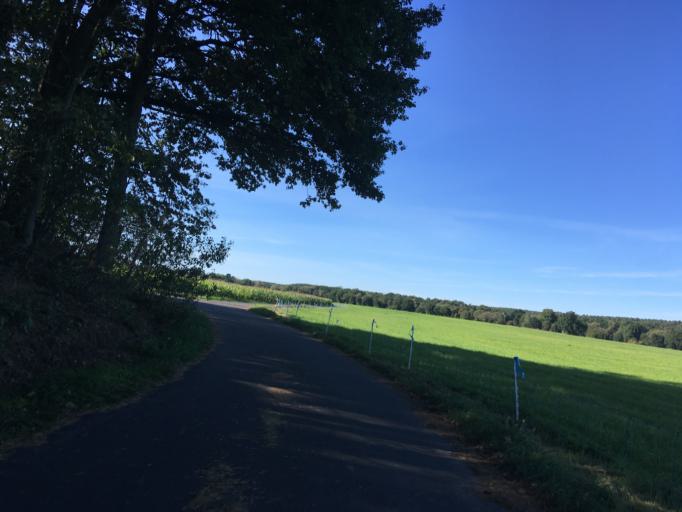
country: PL
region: Lubusz
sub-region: Powiat zarski
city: Przewoz
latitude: 51.4784
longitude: 14.9181
